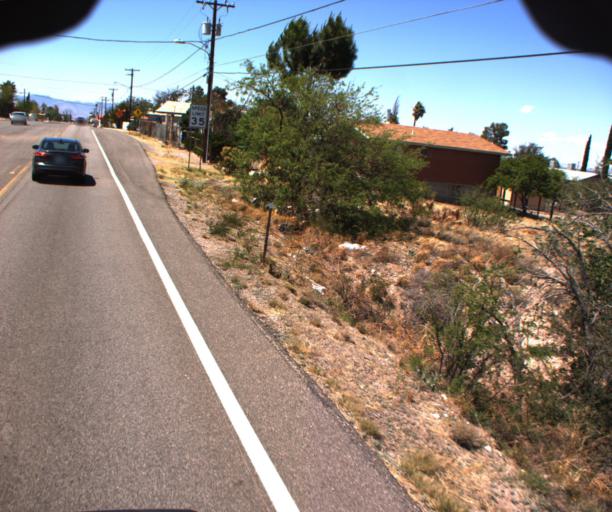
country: US
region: Arizona
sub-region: Cochise County
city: Tombstone
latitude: 31.7110
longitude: -110.0591
